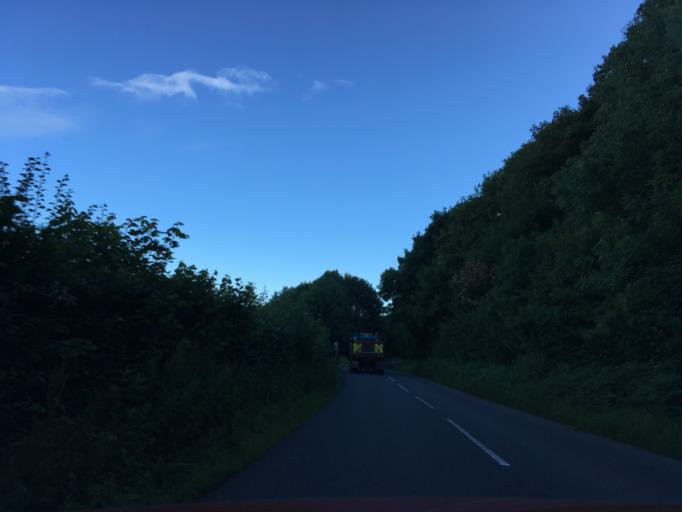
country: GB
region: Wales
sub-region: Monmouthshire
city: Tintern
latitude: 51.6769
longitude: -2.7526
